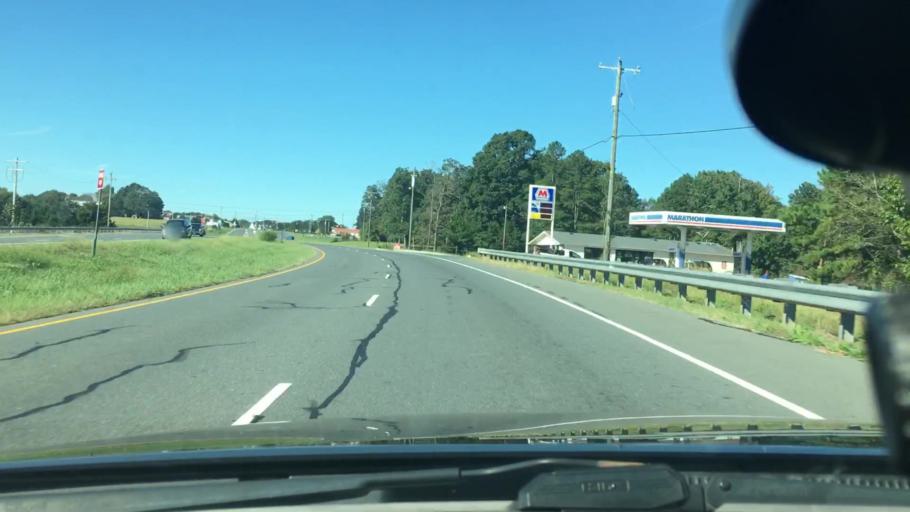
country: US
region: North Carolina
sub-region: Stanly County
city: Oakboro
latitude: 35.2693
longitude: -80.3473
